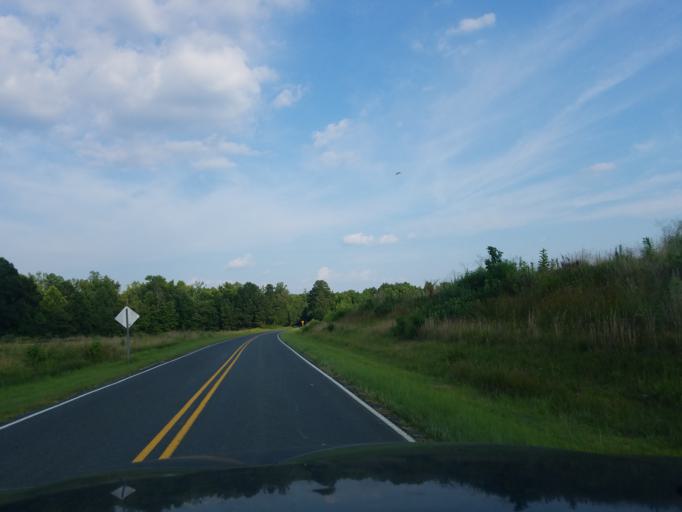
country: US
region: North Carolina
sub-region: Granville County
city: Butner
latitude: 36.1995
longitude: -78.8449
